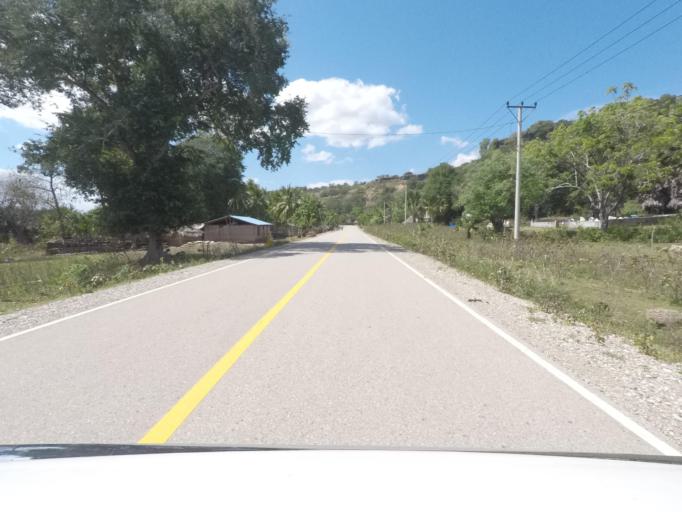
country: TL
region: Lautem
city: Lospalos
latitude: -8.4166
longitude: 126.7937
